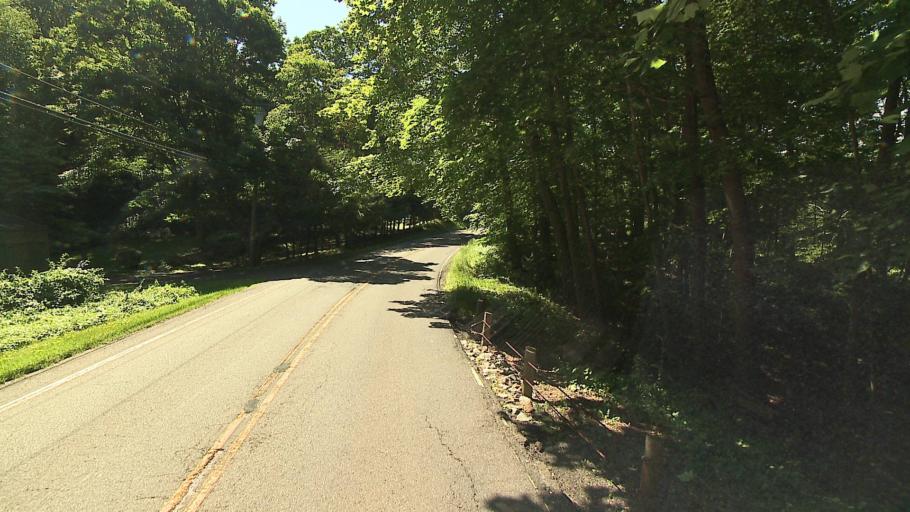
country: US
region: Connecticut
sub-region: Fairfield County
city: Ridgefield
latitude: 41.2927
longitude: -73.5256
